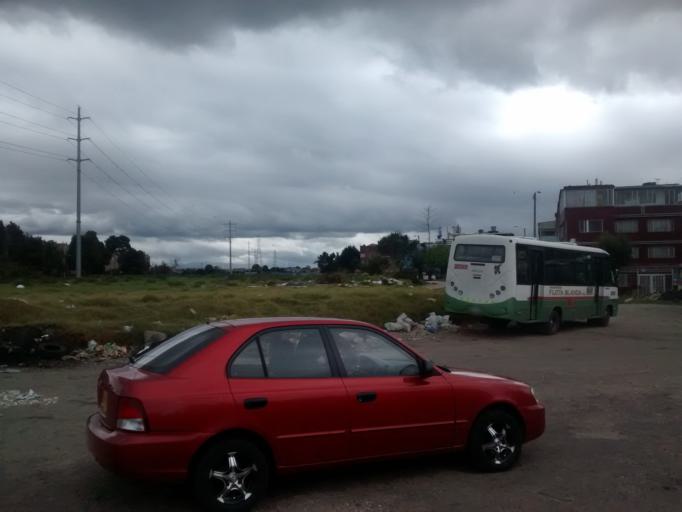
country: CO
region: Cundinamarca
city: Cota
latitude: 4.7149
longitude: -74.1064
